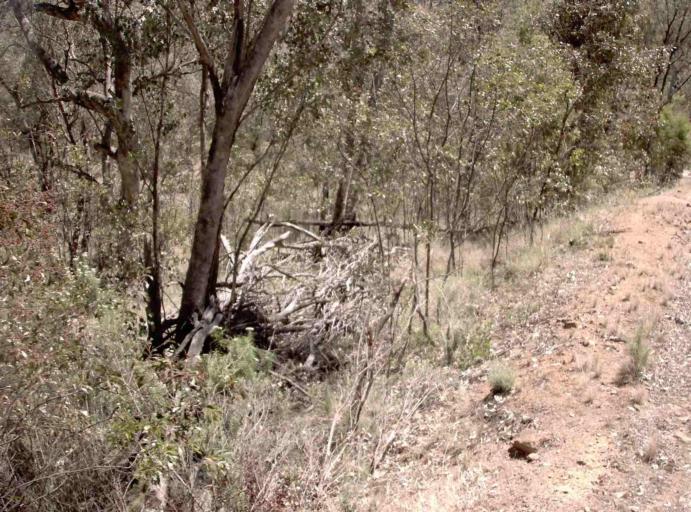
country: AU
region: New South Wales
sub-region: Snowy River
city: Jindabyne
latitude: -36.9412
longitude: 148.3409
